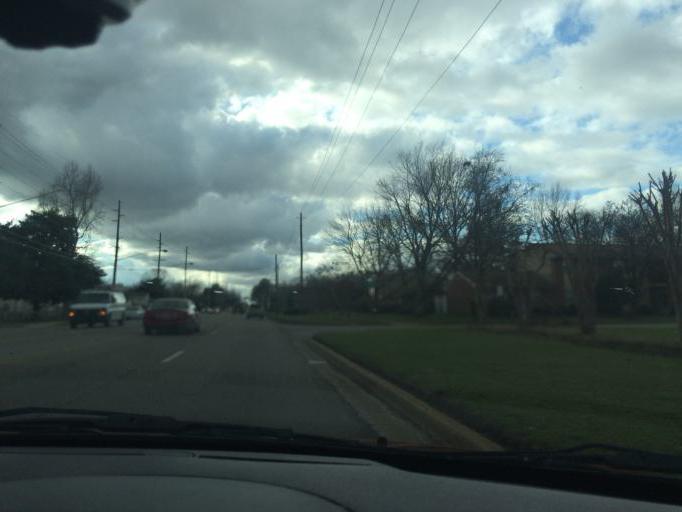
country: US
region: Alabama
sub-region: Madison County
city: Huntsville
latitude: 34.7128
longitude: -86.6149
